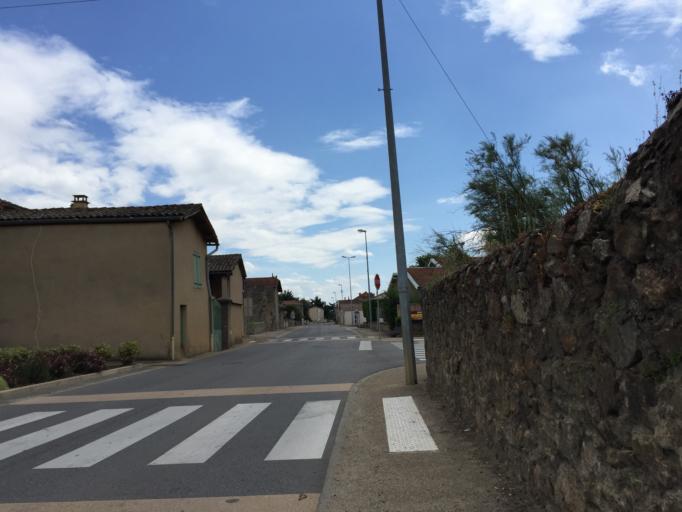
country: FR
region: Rhone-Alpes
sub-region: Departement de la Drome
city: Andancette
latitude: 45.2720
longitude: 4.8001
